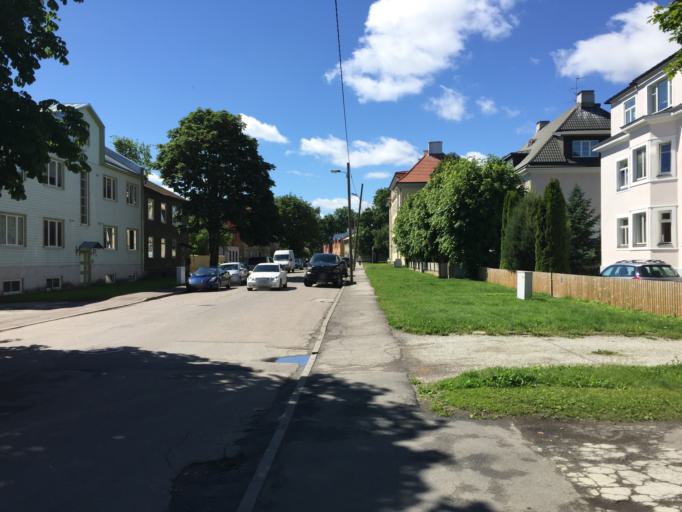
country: EE
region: Harju
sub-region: Tallinna linn
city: Tallinn
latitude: 59.4444
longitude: 24.7311
